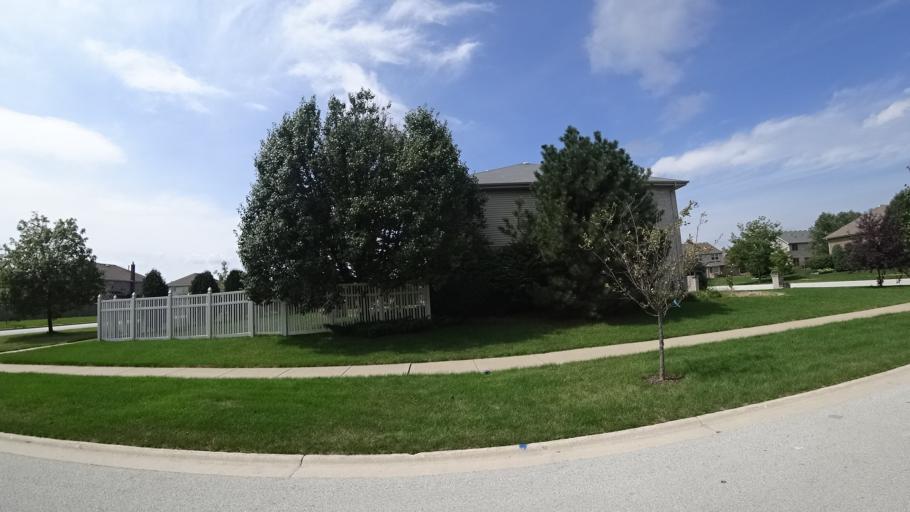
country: US
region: Illinois
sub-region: Cook County
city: Orland Hills
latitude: 41.5656
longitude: -87.8258
